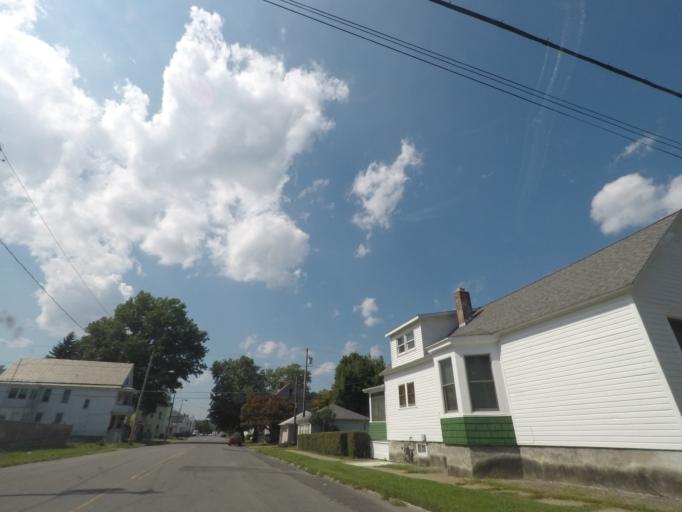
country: US
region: New York
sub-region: Saratoga County
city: Waterford
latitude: 42.7690
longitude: -73.6708
